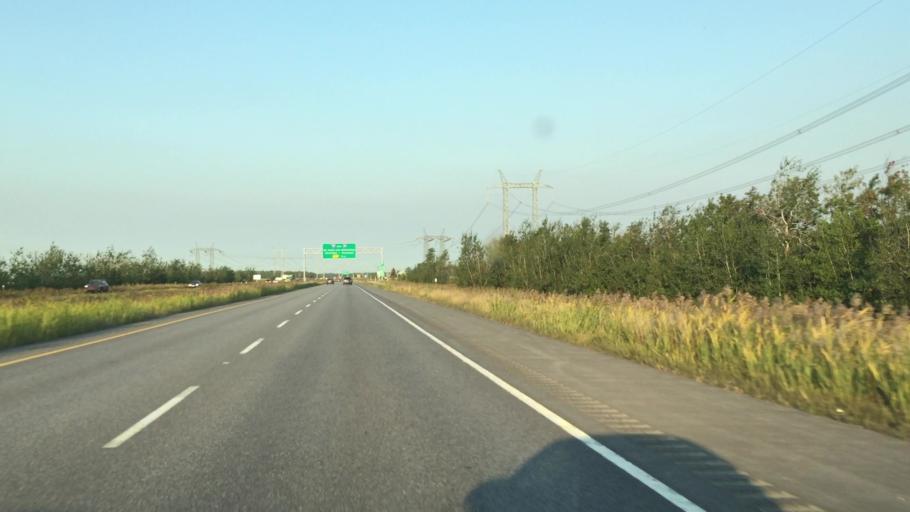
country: CA
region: Quebec
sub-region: Monteregie
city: Richelieu
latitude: 45.4123
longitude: -73.2690
